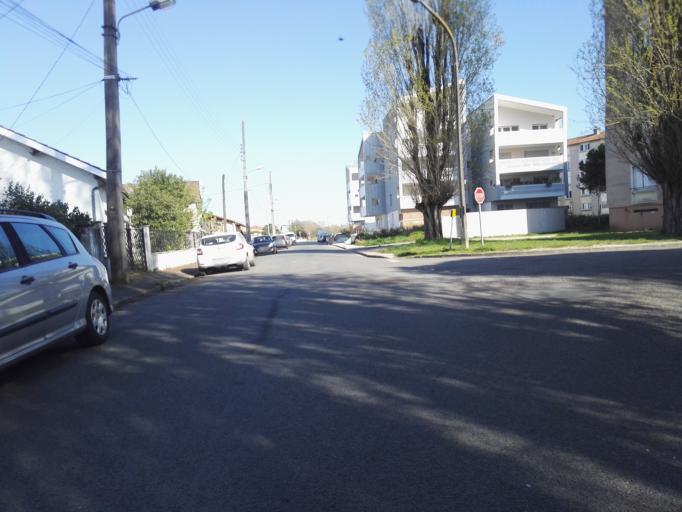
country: FR
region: Aquitaine
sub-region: Departement de la Gironde
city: Begles
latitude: 44.7990
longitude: -0.5531
